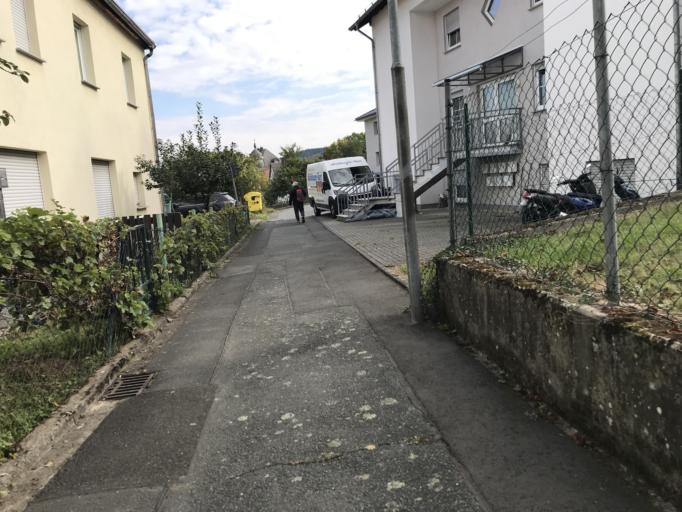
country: DE
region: Hesse
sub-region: Regierungsbezirk Giessen
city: Ehringshausen
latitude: 50.6003
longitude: 8.4152
